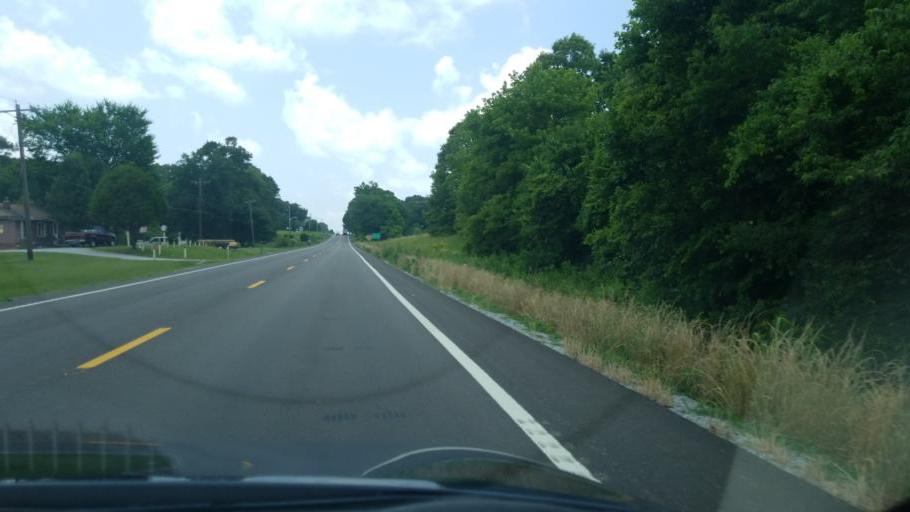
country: US
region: Tennessee
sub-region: Carroll County
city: Huntingdon
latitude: 36.0234
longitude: -88.3679
